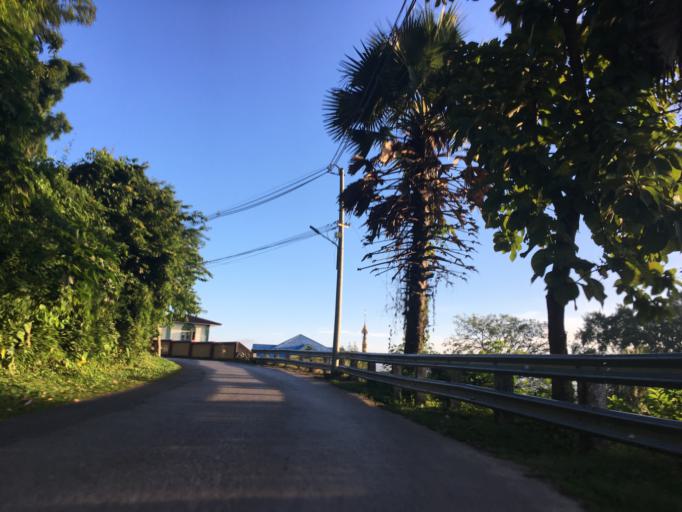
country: MM
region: Mon
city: Mawlamyine
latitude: 16.4702
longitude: 97.6310
